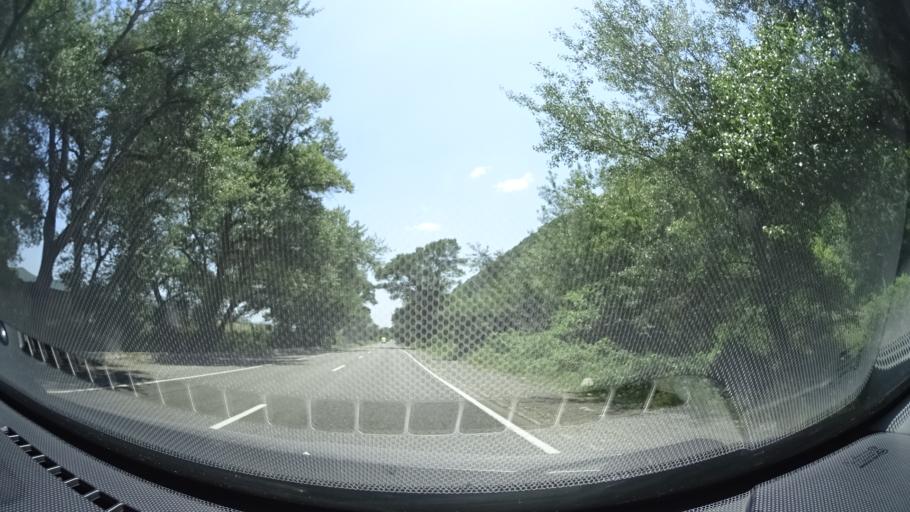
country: GE
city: Zhinvali
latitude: 42.0457
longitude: 44.7451
